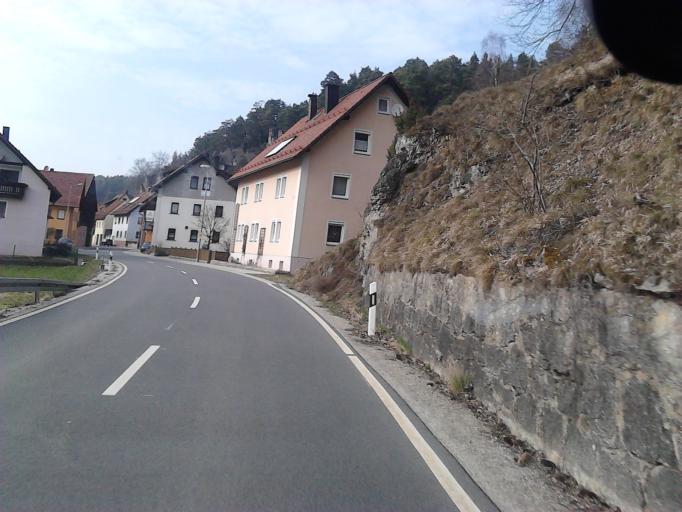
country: DE
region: Bavaria
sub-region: Upper Franconia
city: Stadelhofen
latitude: 49.9640
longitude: 11.2031
